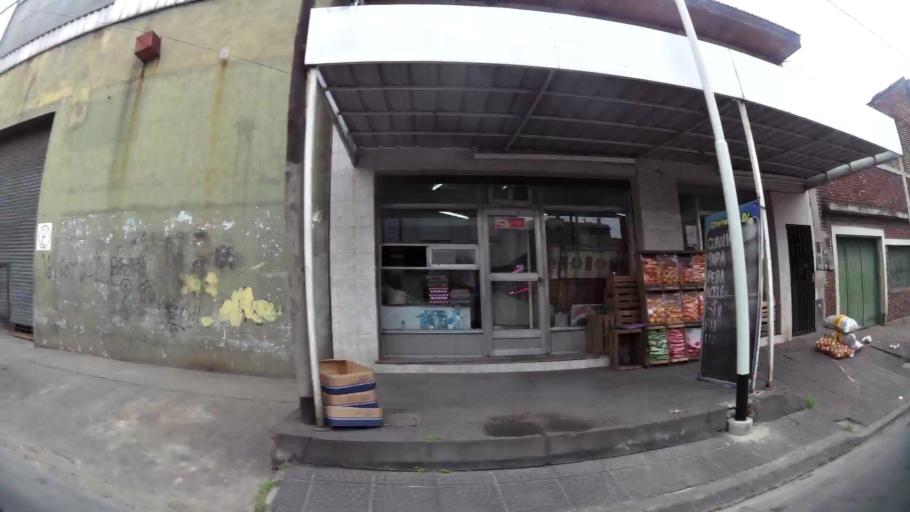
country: AR
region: Buenos Aires
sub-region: Partido de Avellaneda
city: Avellaneda
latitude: -34.6464
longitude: -58.3477
